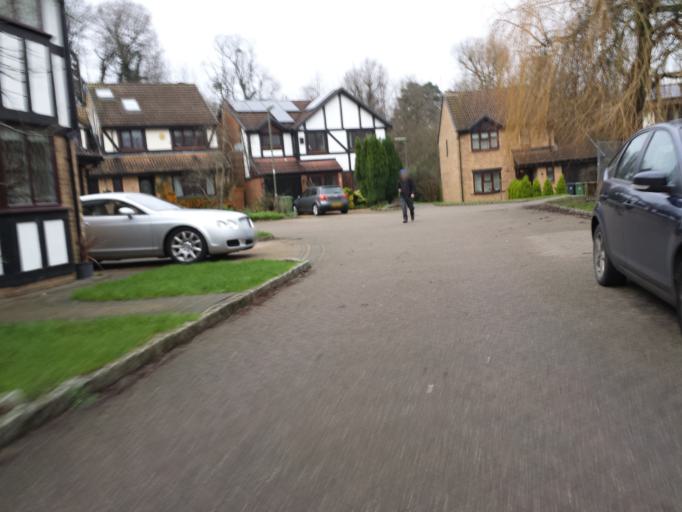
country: GB
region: England
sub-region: Surrey
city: Bagshot
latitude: 51.3568
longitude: -0.6904
